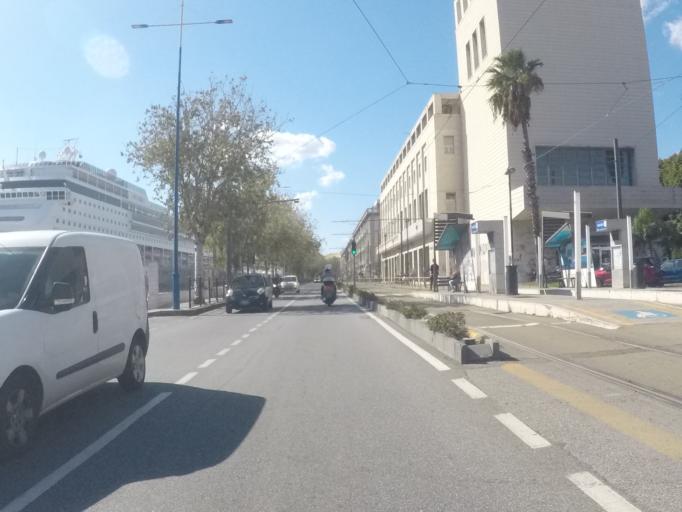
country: IT
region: Sicily
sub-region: Messina
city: Messina
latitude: 38.1939
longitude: 15.5574
